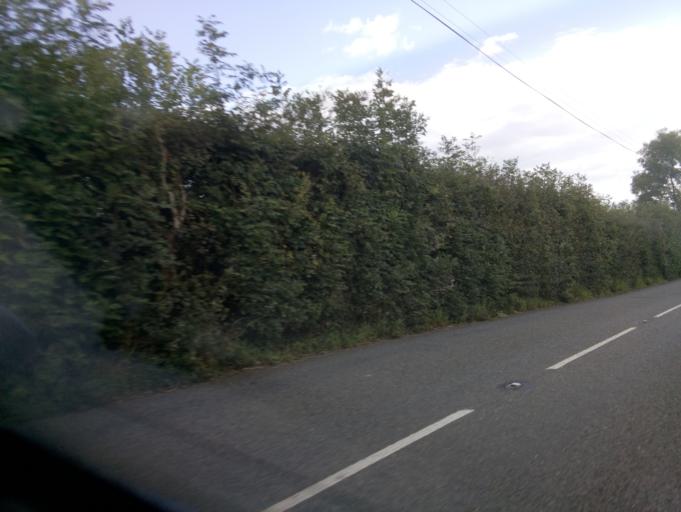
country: GB
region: England
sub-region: Devon
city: Sidmouth
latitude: 50.7297
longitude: -3.2155
